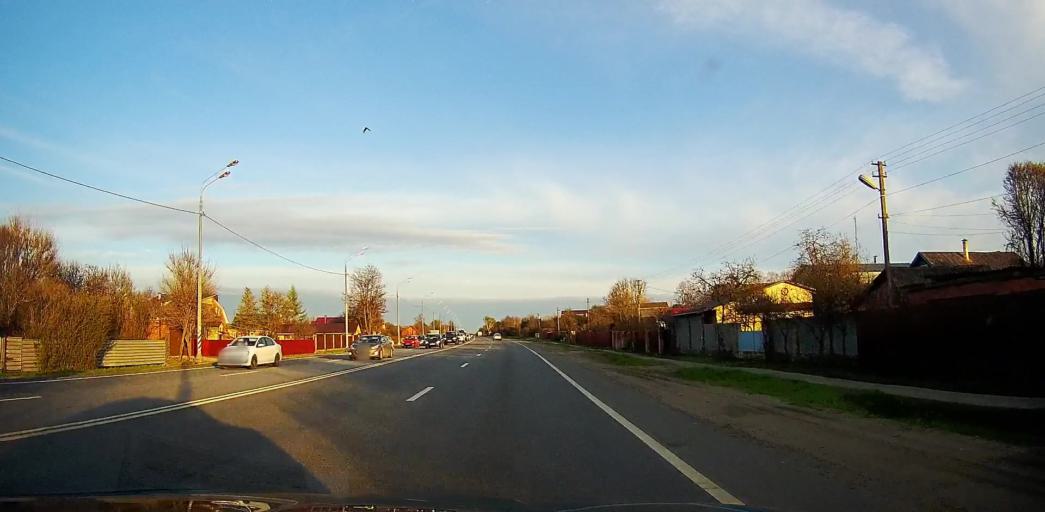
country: RU
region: Moskovskaya
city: Troitskoye
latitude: 55.2460
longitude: 38.5308
